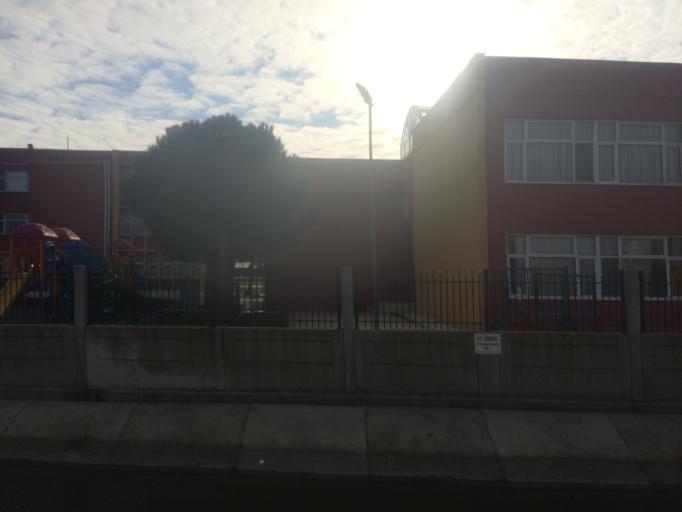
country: TR
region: Izmir
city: Karsiyaka
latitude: 38.4943
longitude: 26.9577
